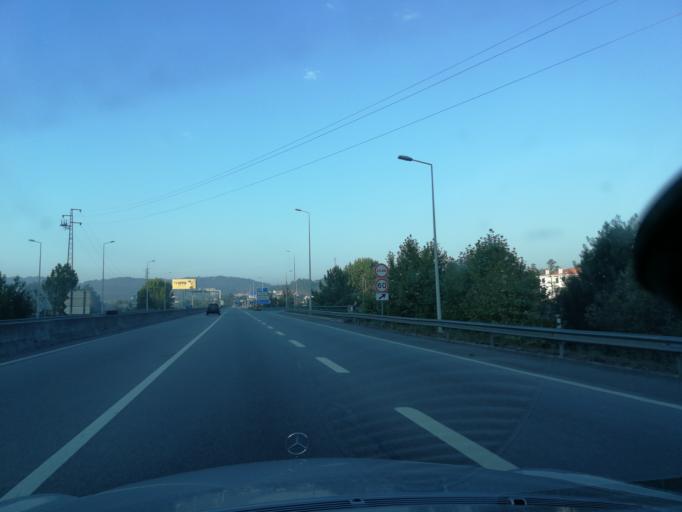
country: PT
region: Braga
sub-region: Braga
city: Braga
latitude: 41.5233
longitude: -8.4182
